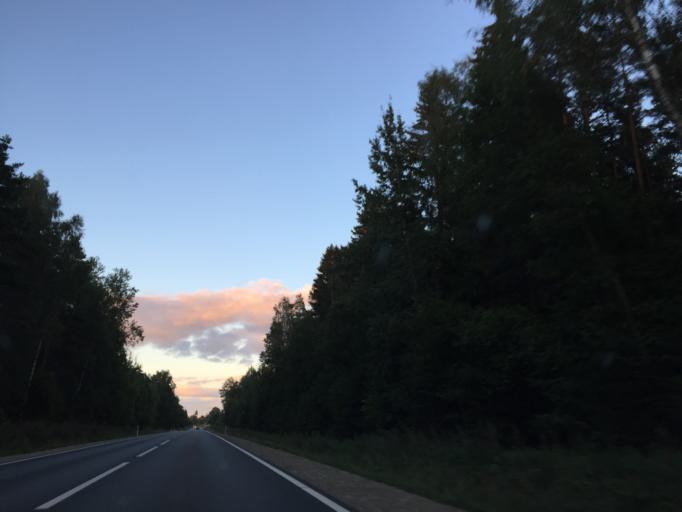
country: LV
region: Jaunpils
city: Jaunpils
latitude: 56.6962
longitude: 23.1431
